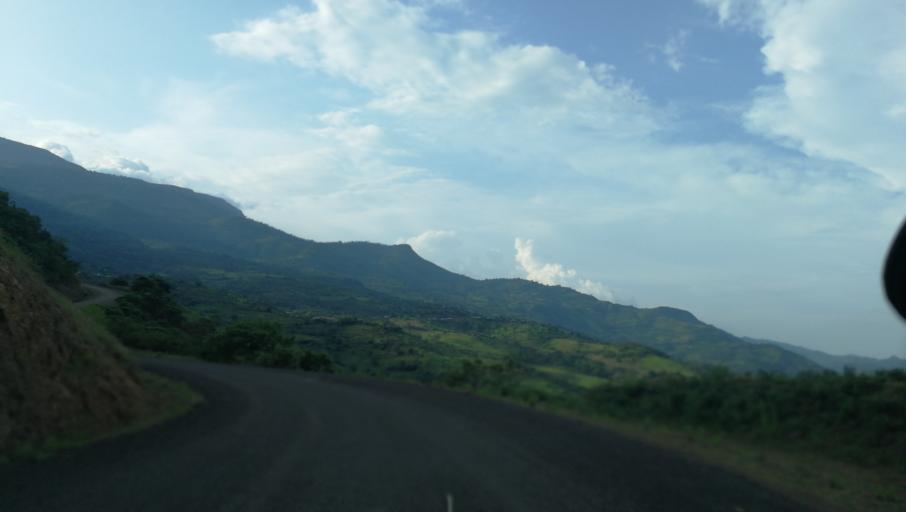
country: ET
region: Southern Nations, Nationalities, and People's Region
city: Areka
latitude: 6.8509
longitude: 37.2700
